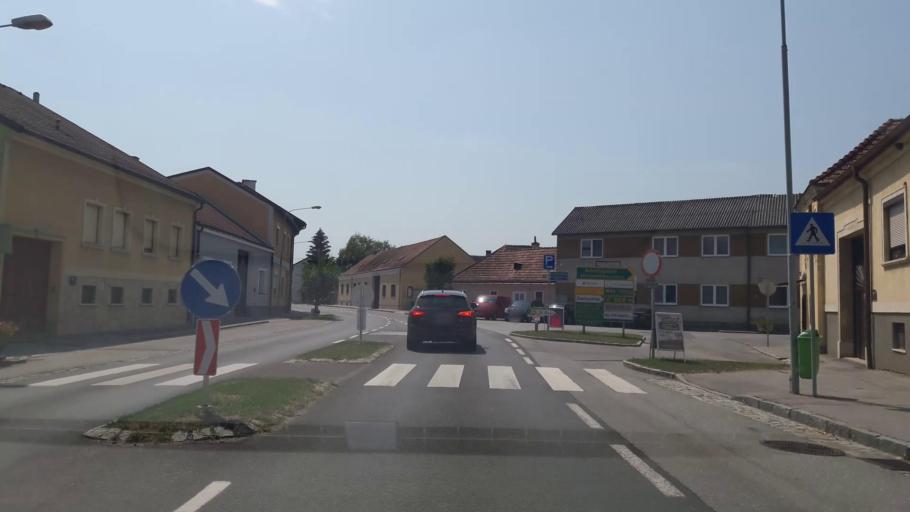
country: AT
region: Lower Austria
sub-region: Politischer Bezirk Wien-Umgebung
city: Schwadorf
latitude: 48.0472
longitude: 16.6035
